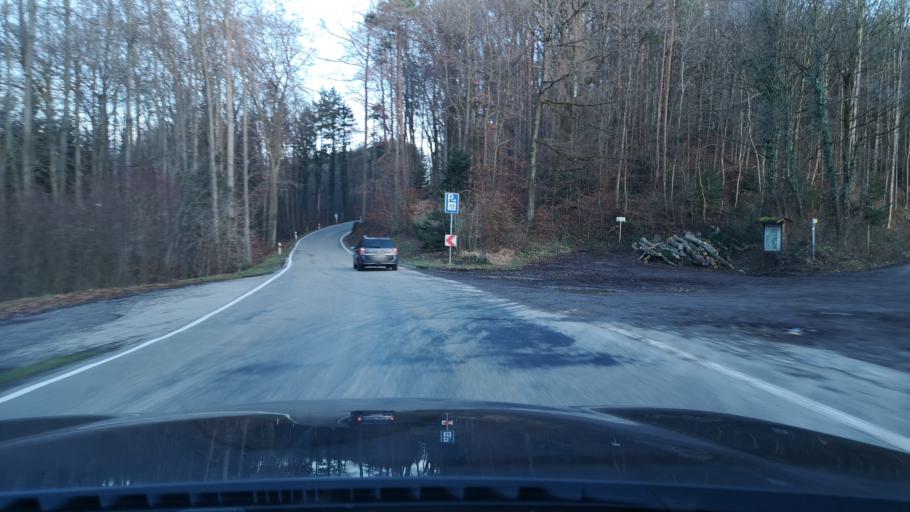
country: DE
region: Baden-Wuerttemberg
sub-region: Regierungsbezirk Stuttgart
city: Rudersberg
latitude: 48.9034
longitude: 9.5188
